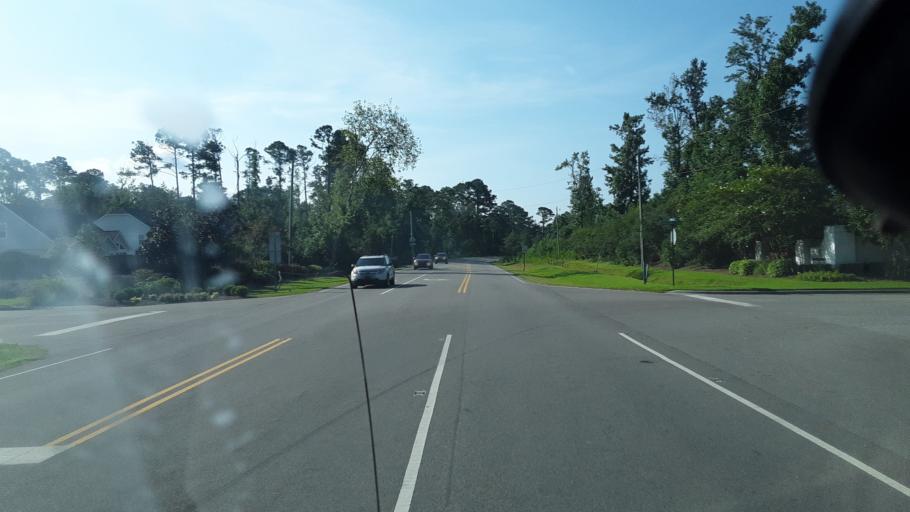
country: US
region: North Carolina
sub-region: Brunswick County
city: Belville
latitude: 34.2193
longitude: -77.9822
